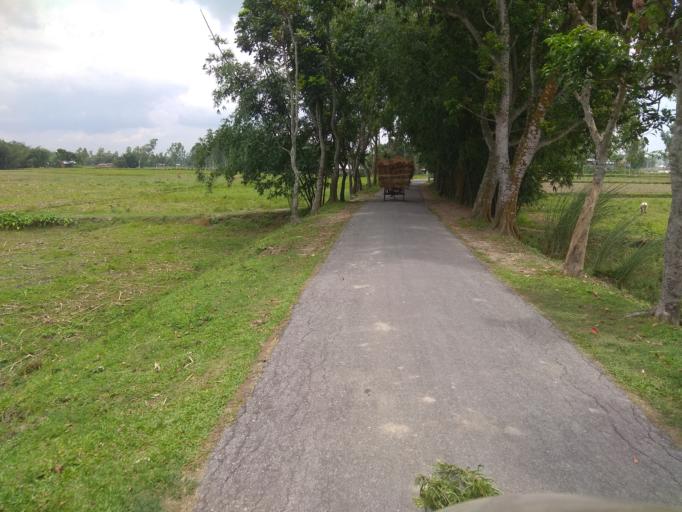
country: IN
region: West Bengal
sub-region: Koch Bihar
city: Haldibari
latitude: 26.2426
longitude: 88.8922
